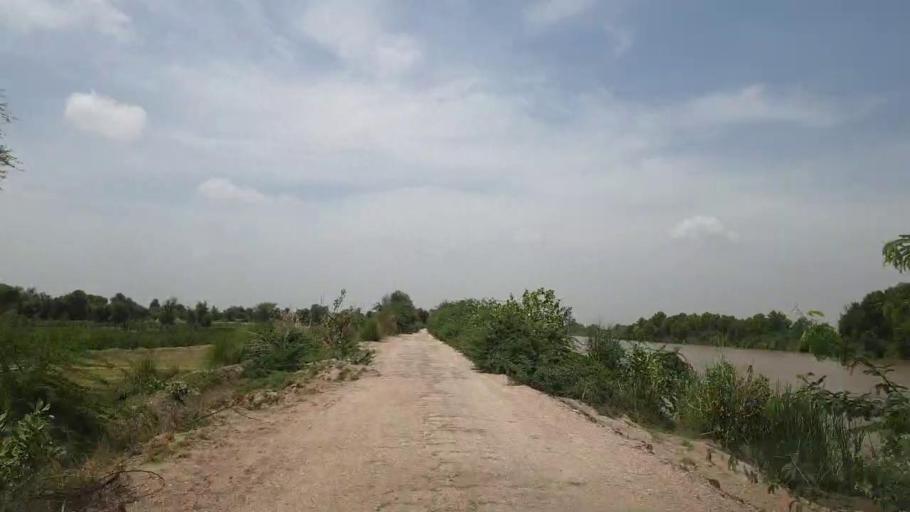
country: PK
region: Sindh
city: Kot Diji
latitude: 27.1318
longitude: 69.0063
